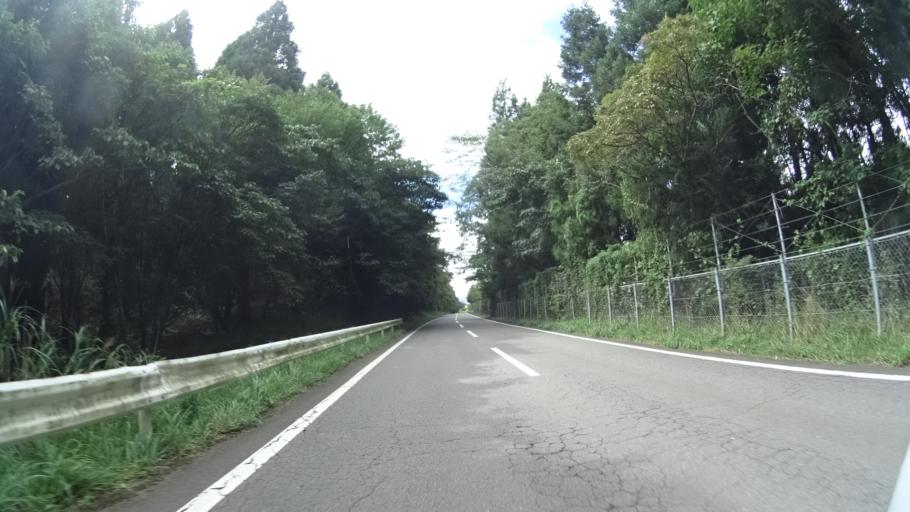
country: JP
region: Oita
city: Beppu
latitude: 33.3339
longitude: 131.4244
